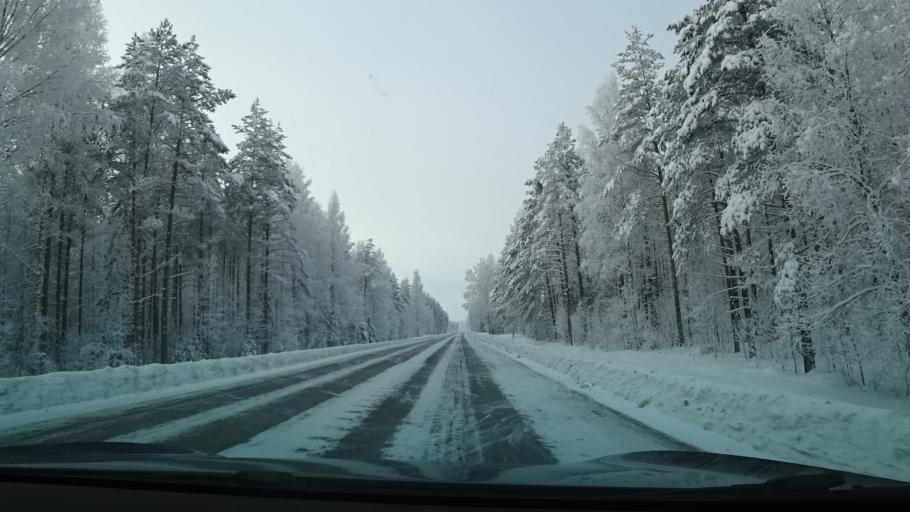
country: FI
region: South Karelia
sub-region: Imatra
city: Saari
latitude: 61.7820
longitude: 29.7093
